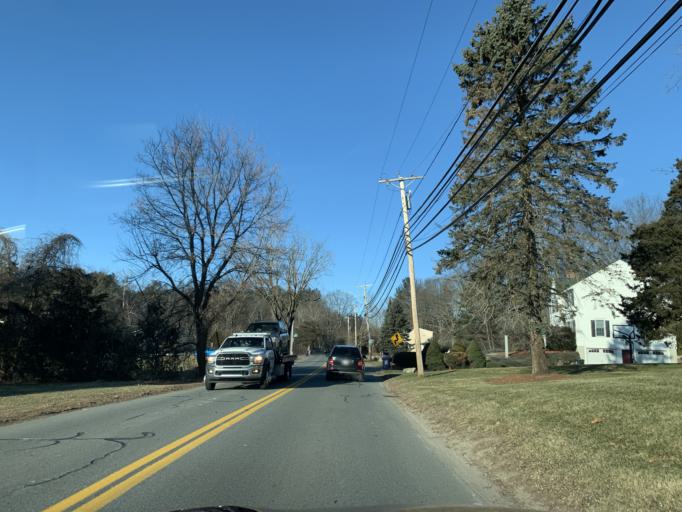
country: US
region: Massachusetts
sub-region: Middlesex County
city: Dracut
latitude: 42.7084
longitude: -71.2529
